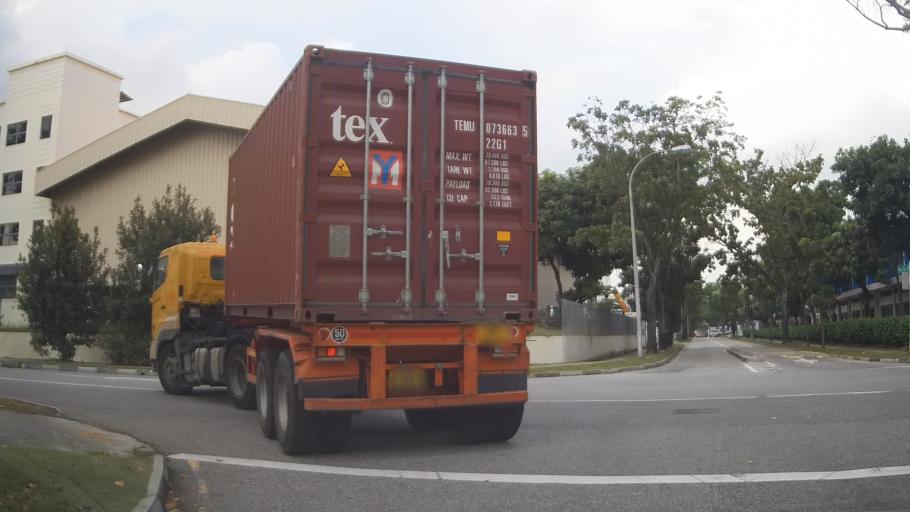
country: MY
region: Johor
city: Johor Bahru
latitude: 1.3221
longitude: 103.6411
